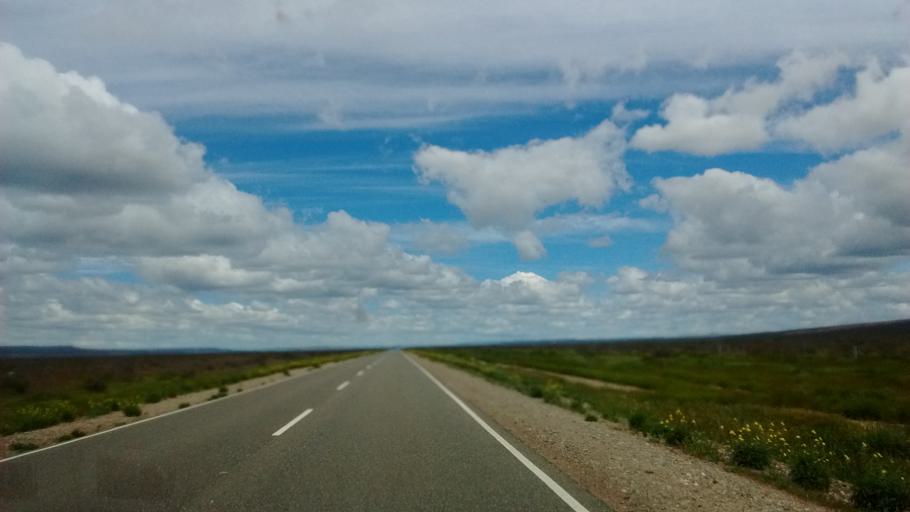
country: AR
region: Neuquen
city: Piedra del Aguila
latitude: -39.7934
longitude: -69.6792
